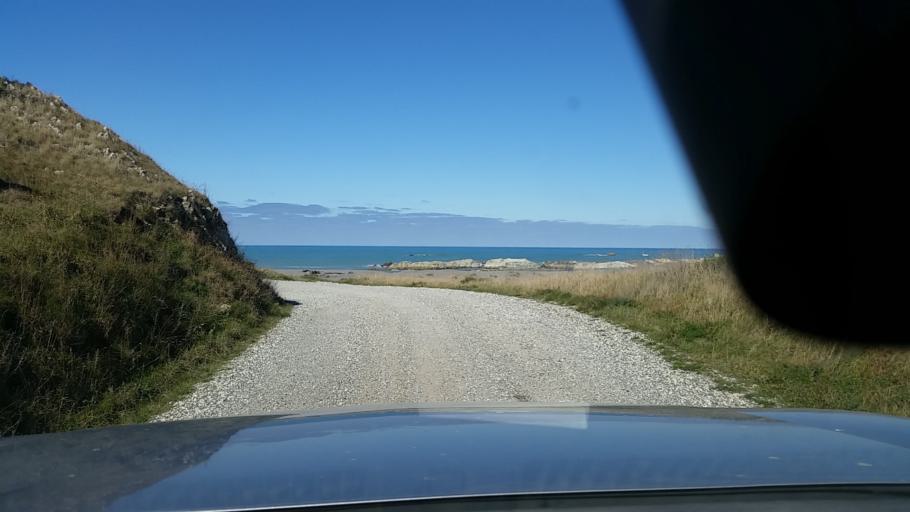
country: NZ
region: Marlborough
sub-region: Marlborough District
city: Blenheim
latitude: -41.8437
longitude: 174.1821
